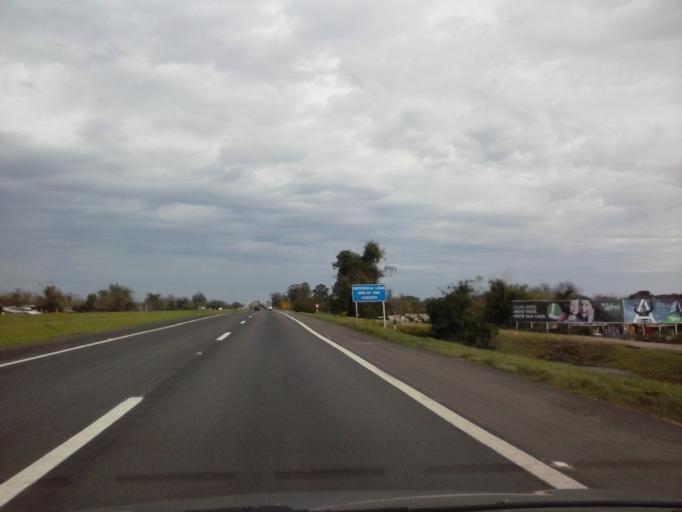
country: BR
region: Rio Grande do Sul
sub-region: Porto Alegre
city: Porto Alegre
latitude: -29.9860
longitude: -51.2533
